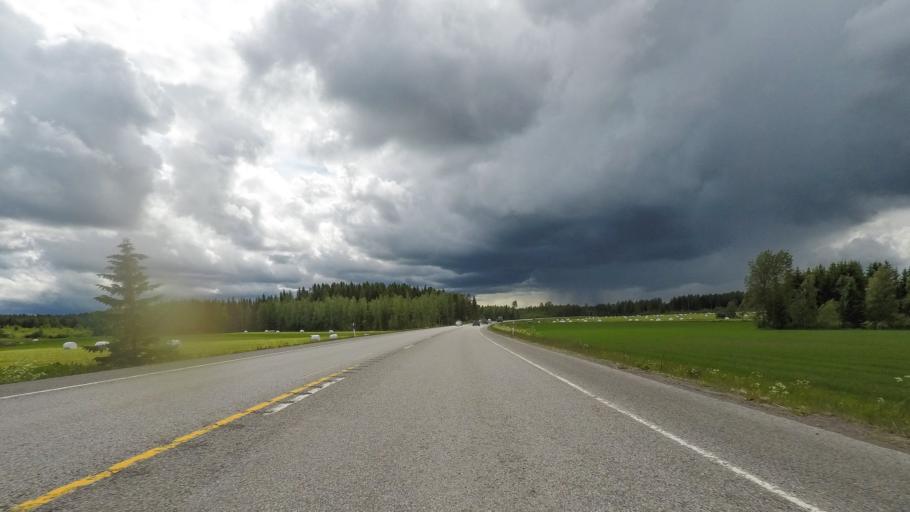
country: FI
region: Central Finland
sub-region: Jyvaeskylae
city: Hankasalmi
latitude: 62.2656
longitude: 26.3246
